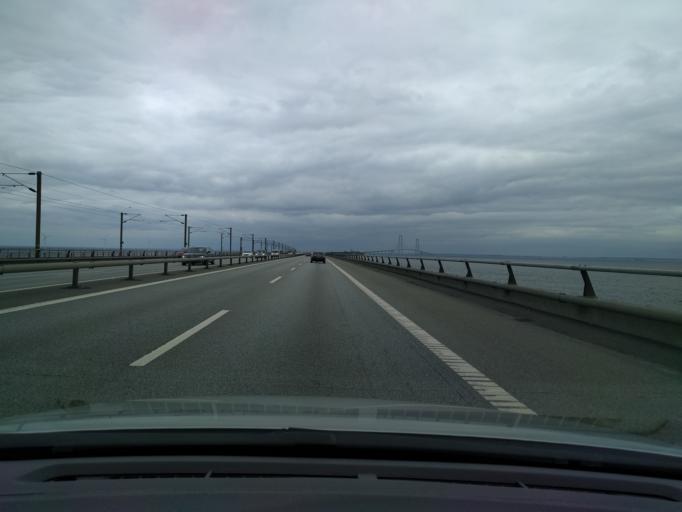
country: DK
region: South Denmark
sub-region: Nyborg Kommune
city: Nyborg
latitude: 55.3179
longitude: 10.9278
